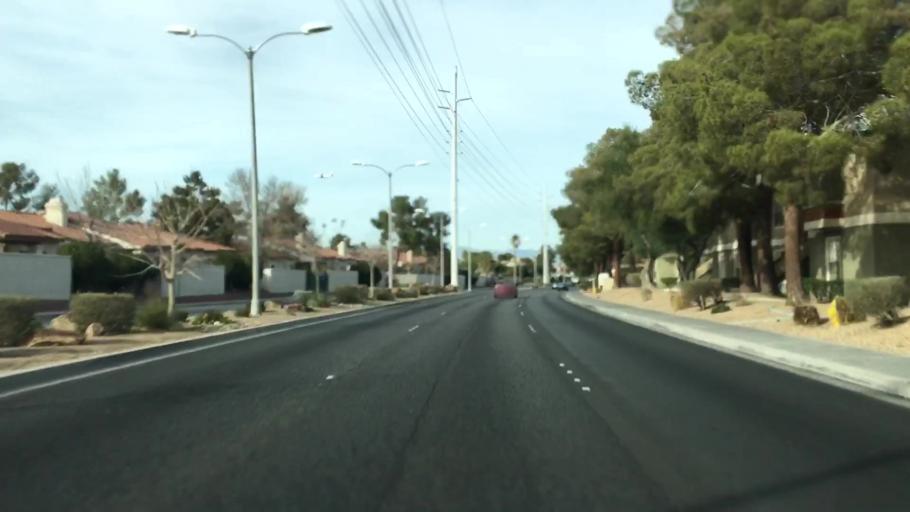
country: US
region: Nevada
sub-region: Clark County
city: Whitney
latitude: 36.0582
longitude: -115.0847
